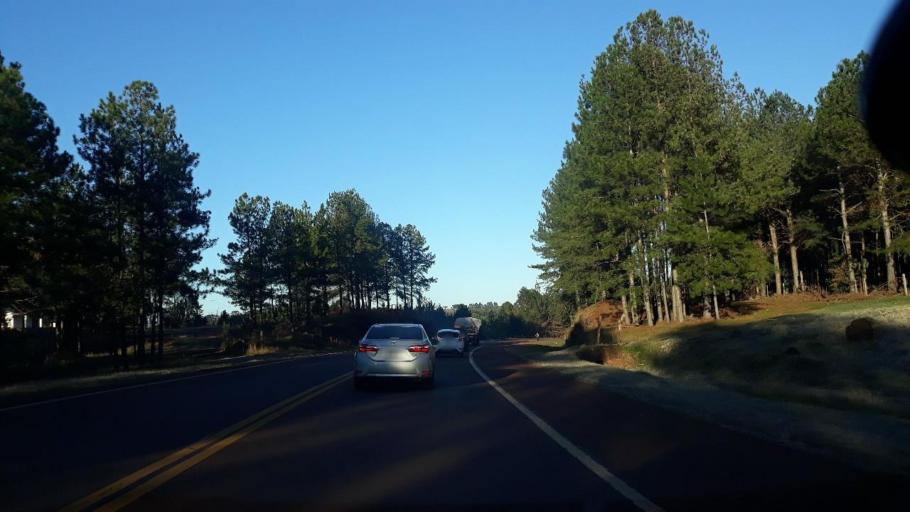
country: AR
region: Misiones
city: San Vicente
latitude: -26.6353
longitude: -54.1269
